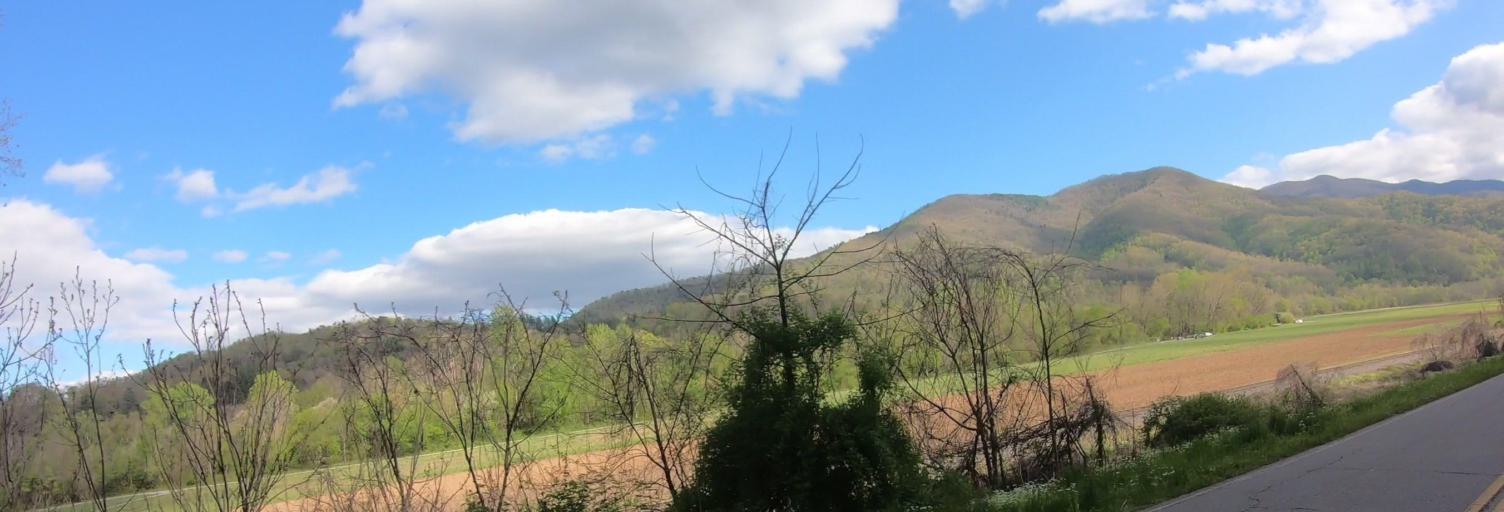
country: US
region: North Carolina
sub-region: Swain County
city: Bryson City
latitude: 35.4424
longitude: -83.4000
